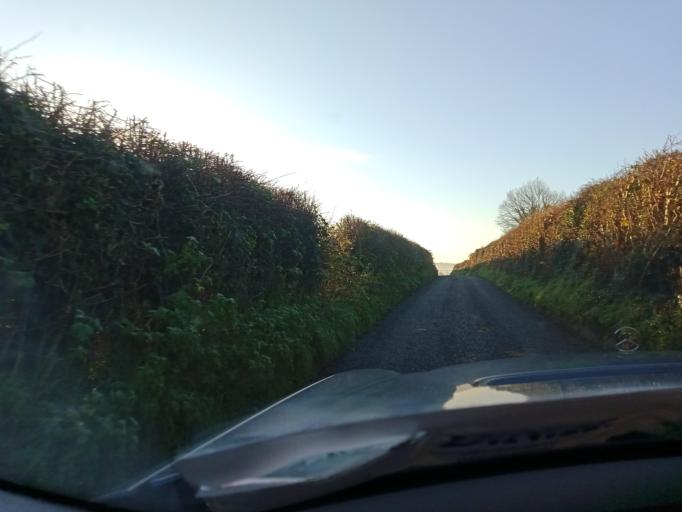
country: IE
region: Leinster
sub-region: Kilkenny
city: Callan
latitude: 52.5133
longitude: -7.4457
